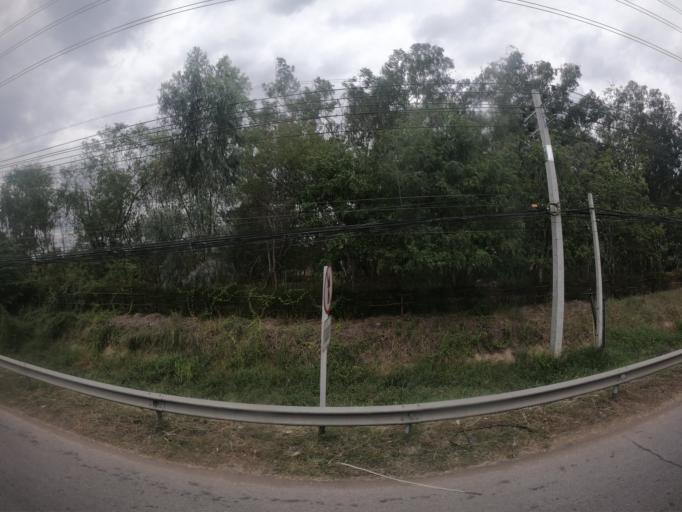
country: TH
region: Nakhon Ratchasima
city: Nakhon Ratchasima
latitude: 14.9241
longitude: 102.1430
